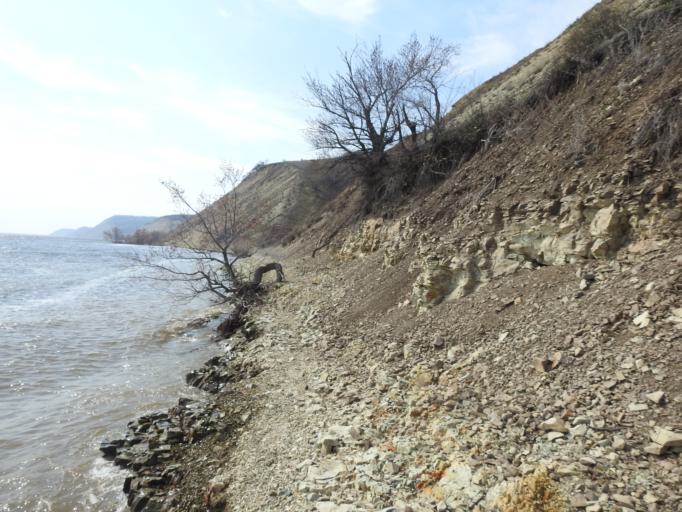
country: RU
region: Saratov
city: Voskresenskoye
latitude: 51.7933
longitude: 46.8609
